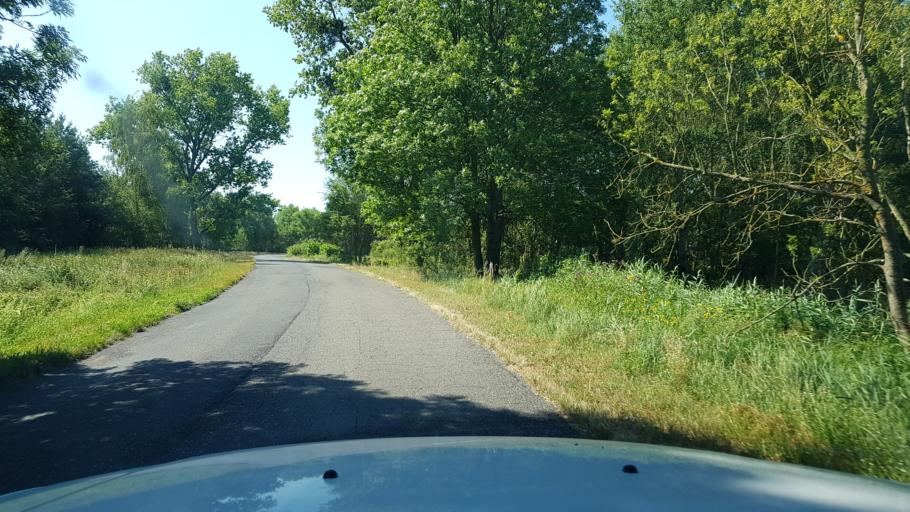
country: PL
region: West Pomeranian Voivodeship
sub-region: Powiat goleniowski
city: Goleniow
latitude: 53.4695
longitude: 14.7153
